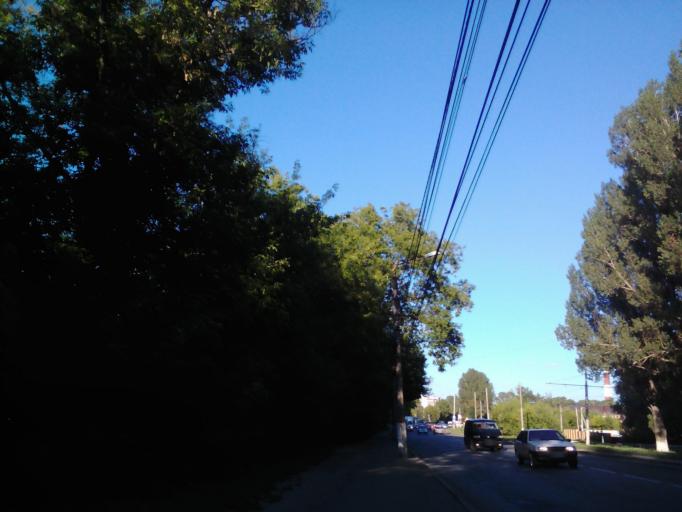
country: RU
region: Kursk
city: Voroshnevo
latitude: 51.6679
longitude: 36.0949
